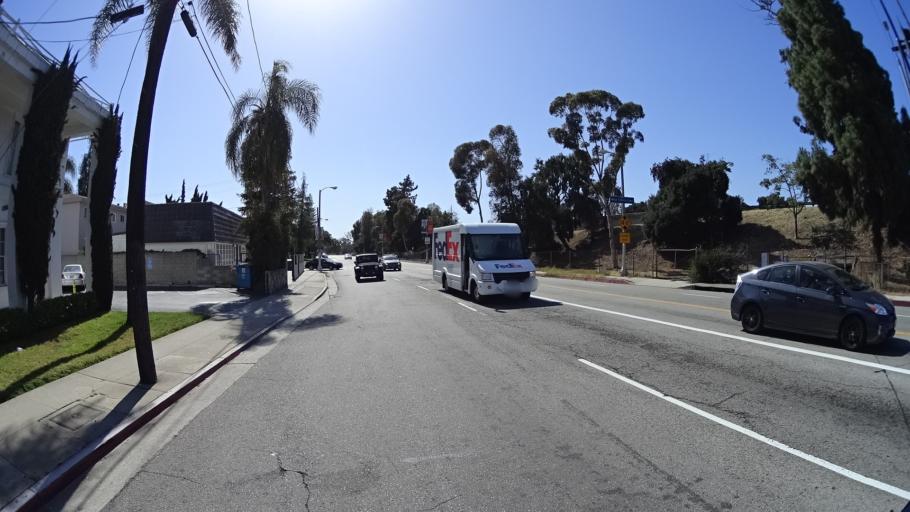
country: US
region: California
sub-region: Los Angeles County
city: North Hollywood
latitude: 34.1524
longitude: -118.3705
